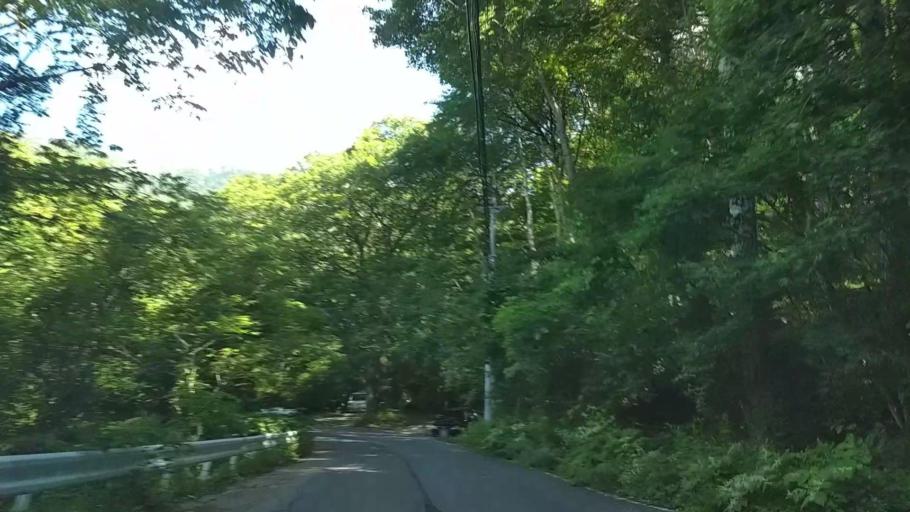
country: JP
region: Nagano
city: Matsumoto
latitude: 36.2107
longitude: 138.1001
